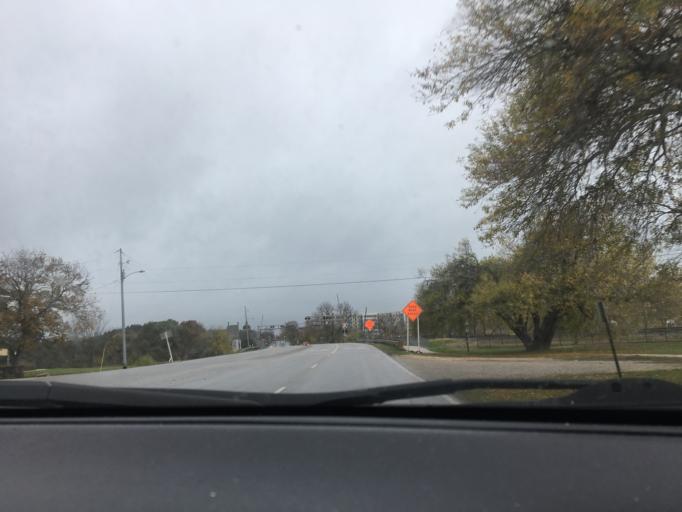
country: US
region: Texas
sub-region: Hays County
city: San Marcos
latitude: 29.8842
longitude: -97.9333
